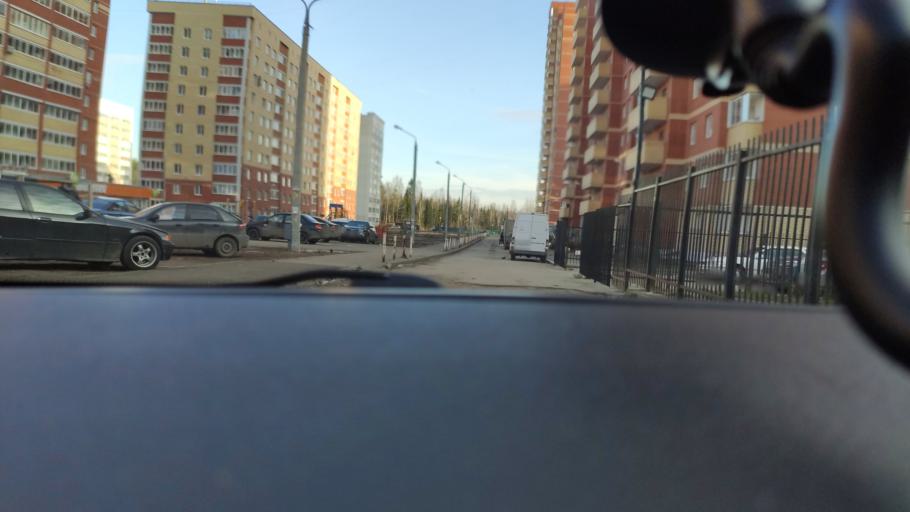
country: RU
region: Perm
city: Kondratovo
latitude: 58.0499
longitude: 56.0865
